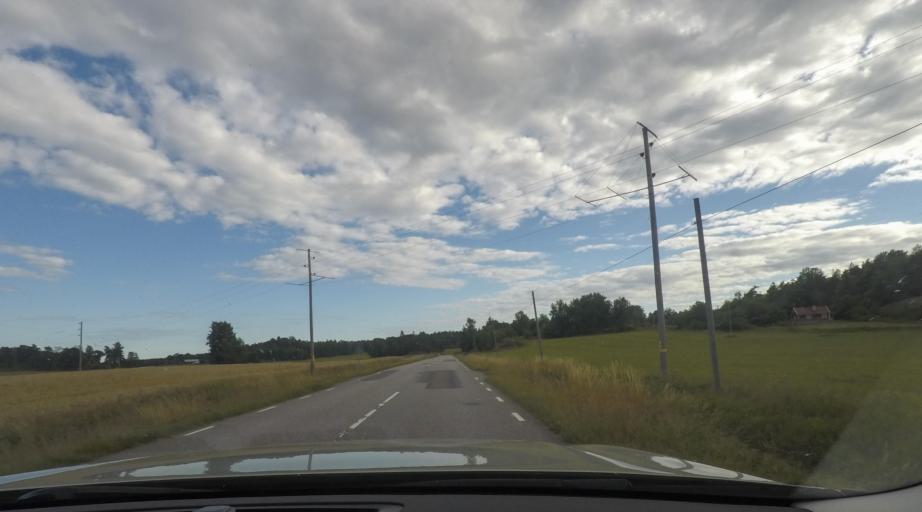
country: SE
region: Soedermanland
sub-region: Trosa Kommun
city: Trosa
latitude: 58.9917
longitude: 17.6765
